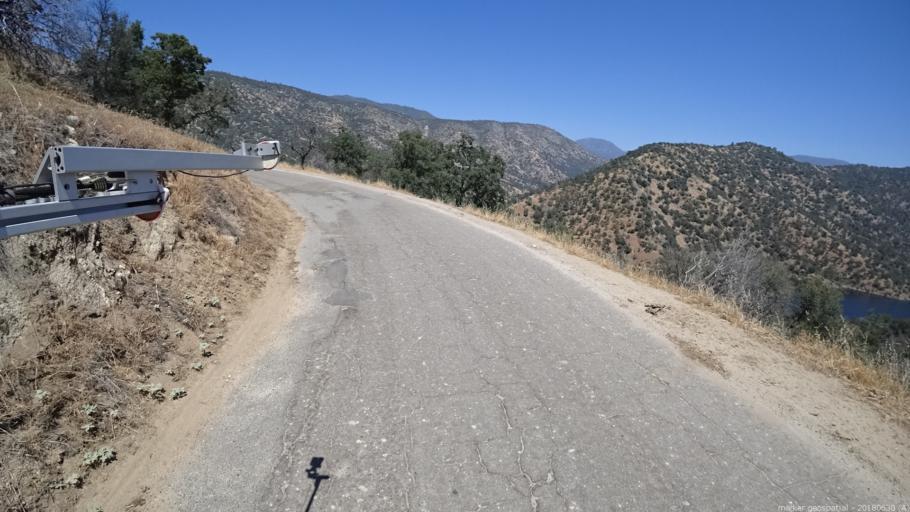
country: US
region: California
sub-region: Fresno County
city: Auberry
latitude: 37.1598
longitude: -119.4389
